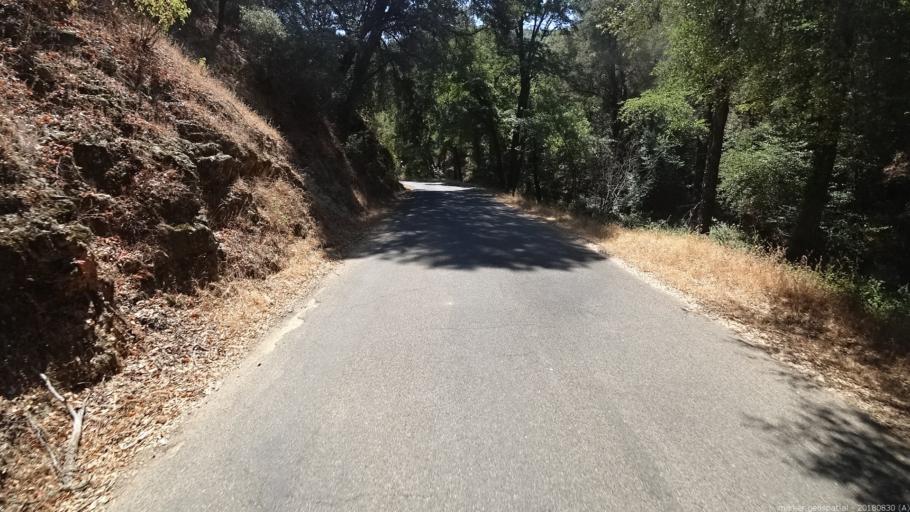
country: US
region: California
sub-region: Monterey County
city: King City
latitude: 36.0053
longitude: -121.3930
